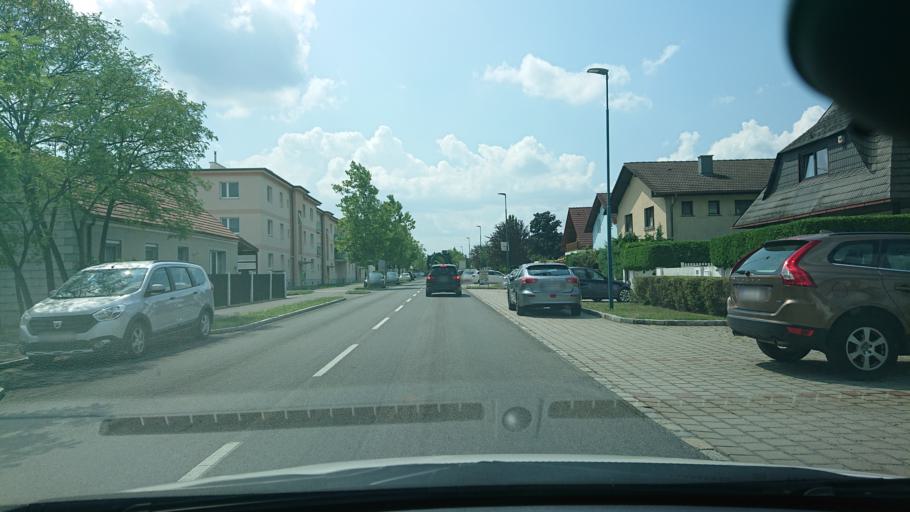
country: AT
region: Lower Austria
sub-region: Politischer Bezirk Baden
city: Kottingbrunn
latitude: 47.9402
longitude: 16.2209
